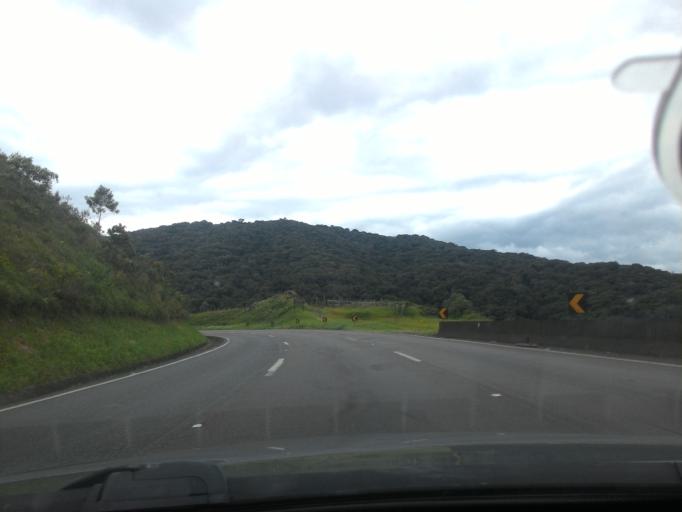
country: BR
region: Sao Paulo
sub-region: Cajati
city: Cajati
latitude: -24.9484
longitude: -48.4236
